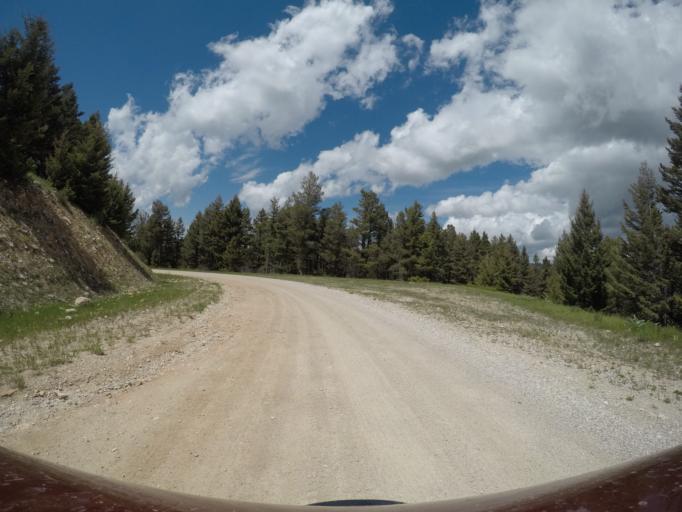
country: US
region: Wyoming
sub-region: Big Horn County
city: Lovell
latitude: 45.1928
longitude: -108.4801
